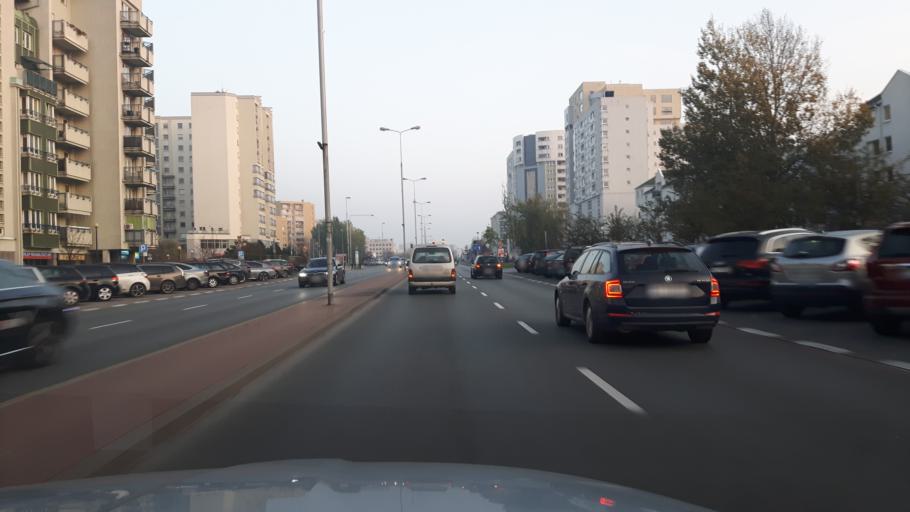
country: PL
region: Masovian Voivodeship
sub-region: Warszawa
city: Ursynow
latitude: 52.1576
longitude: 21.0321
